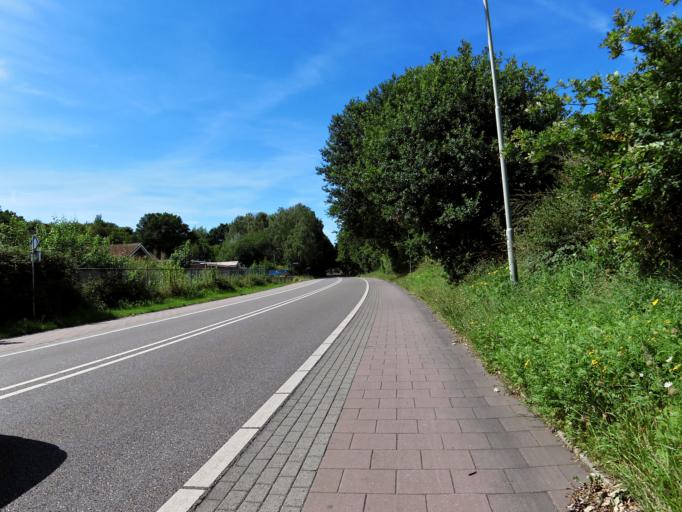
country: NL
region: Limburg
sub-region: Gemeente Kerkrade
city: Kerkrade
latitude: 50.8965
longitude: 6.0344
